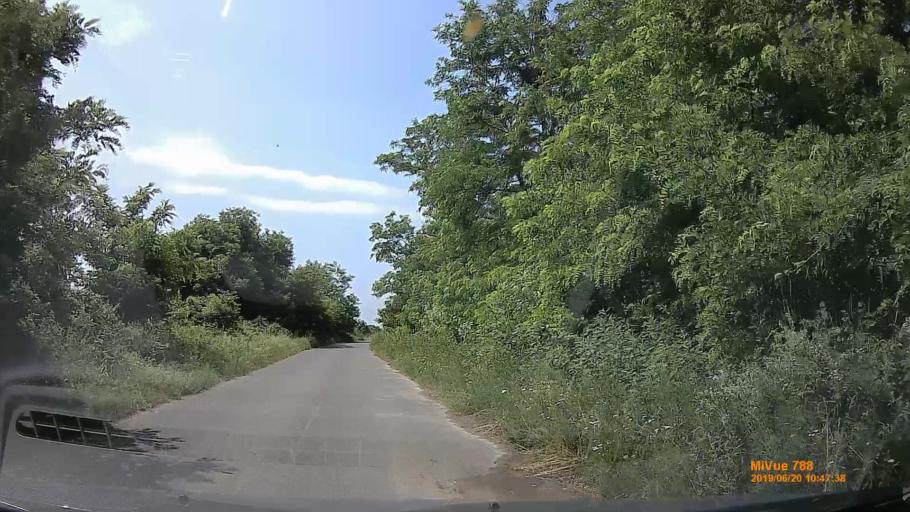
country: HU
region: Baranya
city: Hidas
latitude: 46.1747
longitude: 18.5824
